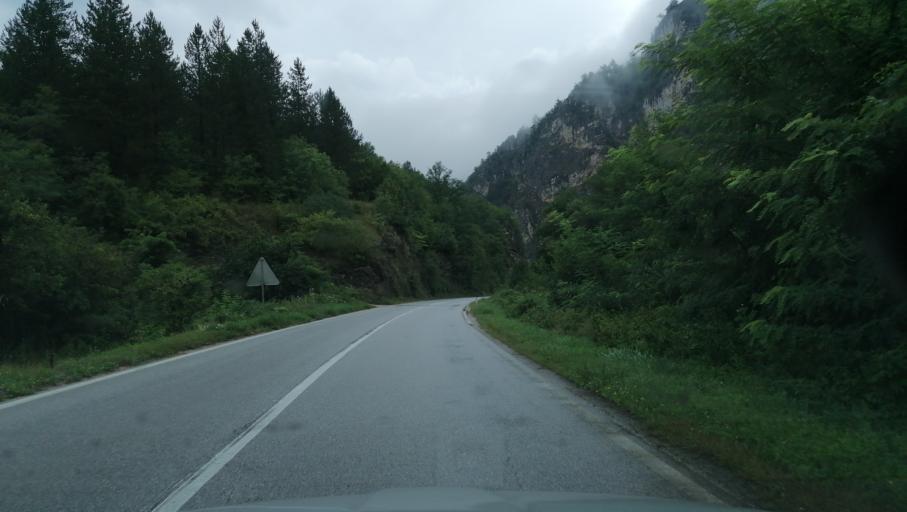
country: RS
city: Durici
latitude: 43.7503
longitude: 19.4001
